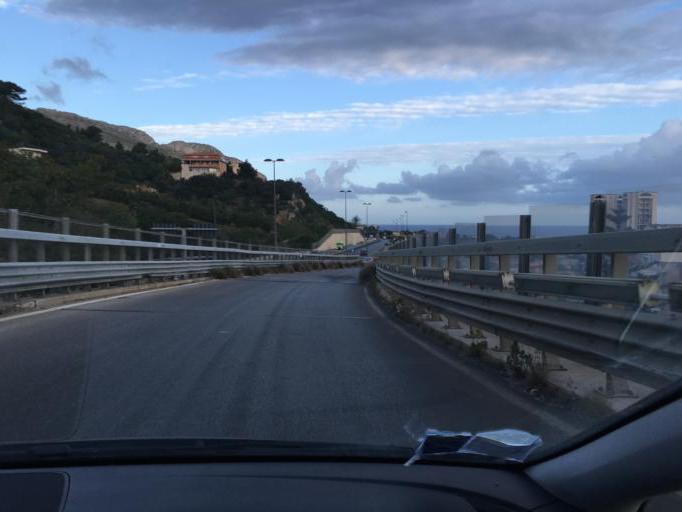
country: IT
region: Sicily
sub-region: Palermo
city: Isola delle Femmine
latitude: 38.1912
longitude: 13.2824
